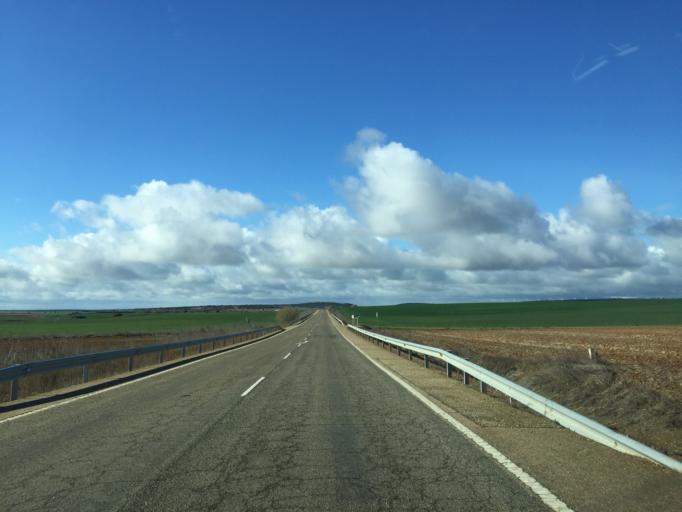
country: ES
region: Castille and Leon
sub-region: Provincia de Zamora
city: San Cebrian de Castro
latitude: 41.7207
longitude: -5.7858
